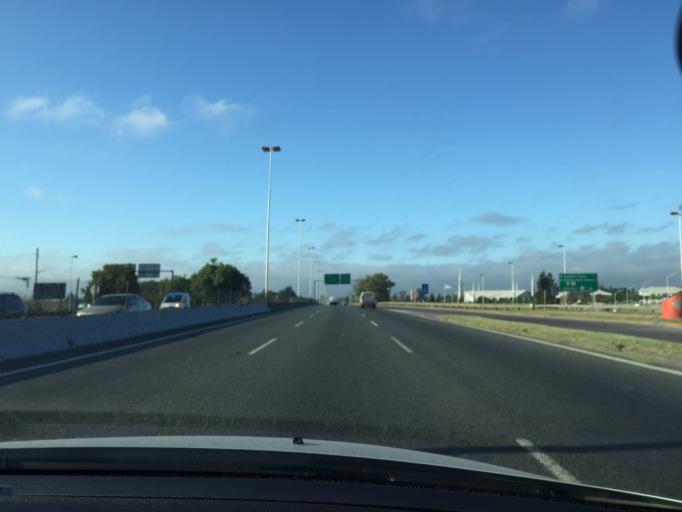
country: AR
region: Buenos Aires F.D.
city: Villa Lugano
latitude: -34.7250
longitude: -58.5148
